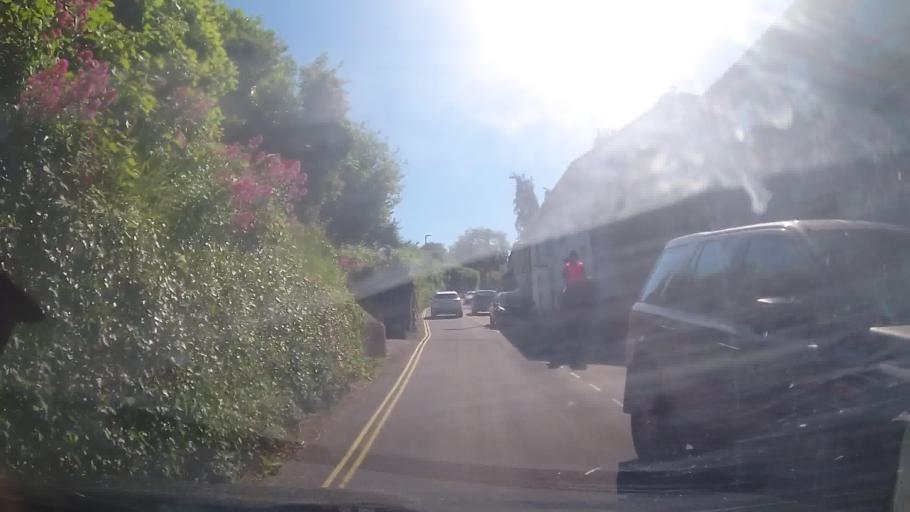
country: GB
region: England
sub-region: Borough of Torbay
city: Brixham
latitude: 50.3811
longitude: -3.5289
